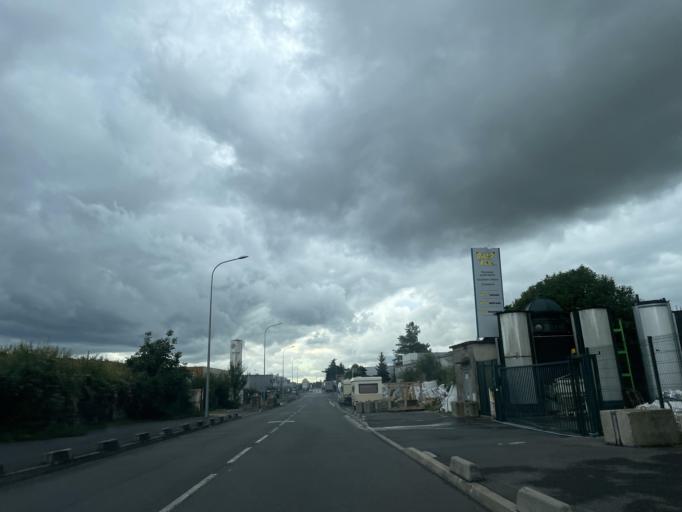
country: FR
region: Ile-de-France
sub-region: Departement de Seine-et-Marne
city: Fublaines
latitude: 48.9599
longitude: 2.9201
